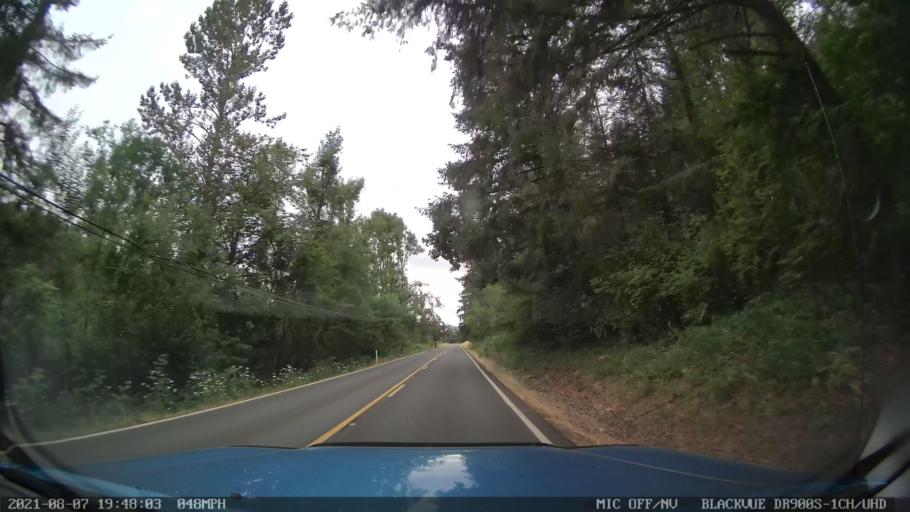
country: US
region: Oregon
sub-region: Marion County
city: Silverton
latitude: 44.9699
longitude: -122.7138
